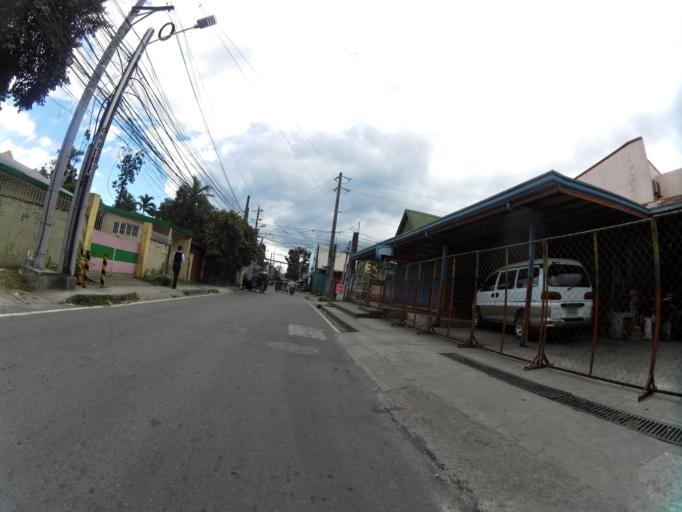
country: PH
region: Calabarzon
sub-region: Province of Rizal
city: Antipolo
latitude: 14.6291
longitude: 121.1080
